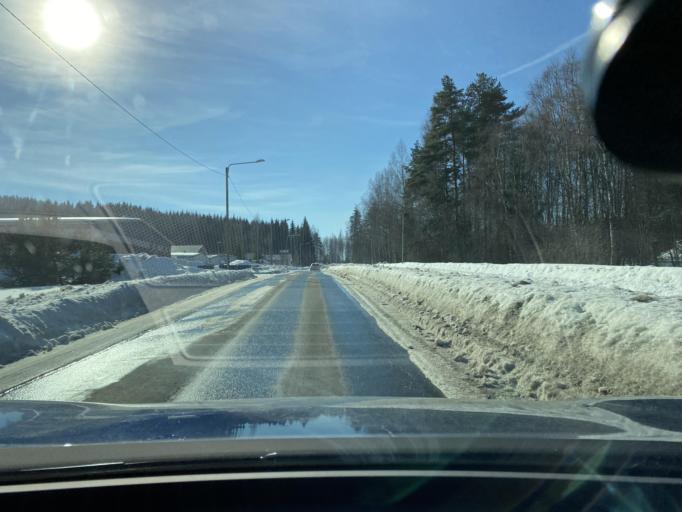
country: FI
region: Central Finland
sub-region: Jyvaeskylae
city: Muurame
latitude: 62.1002
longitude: 25.6467
